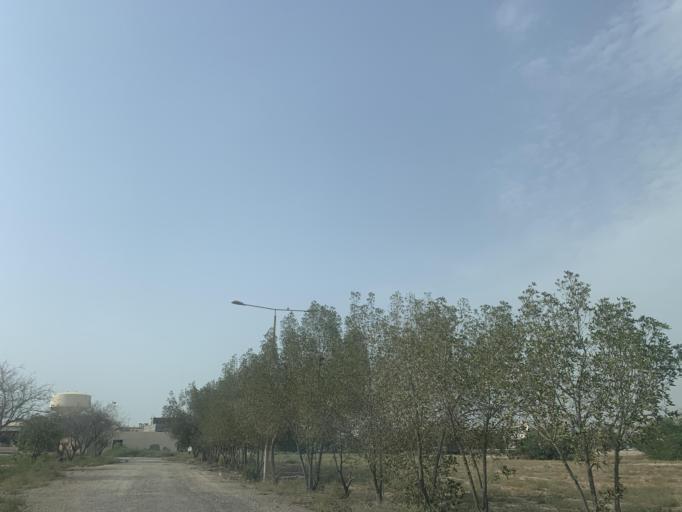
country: BH
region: Northern
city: Madinat `Isa
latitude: 26.1887
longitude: 50.4889
